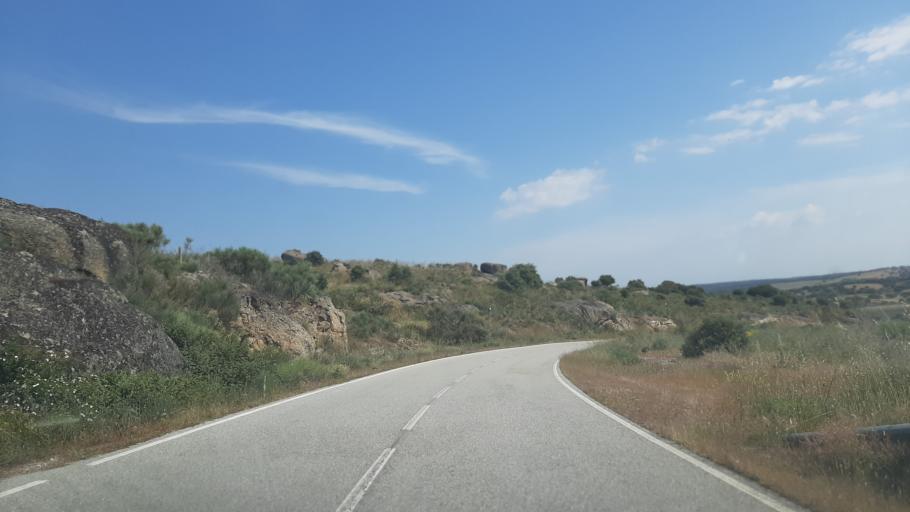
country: ES
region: Castille and Leon
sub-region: Provincia de Salamanca
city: Aldea del Obispo
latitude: 40.6471
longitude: -6.7827
